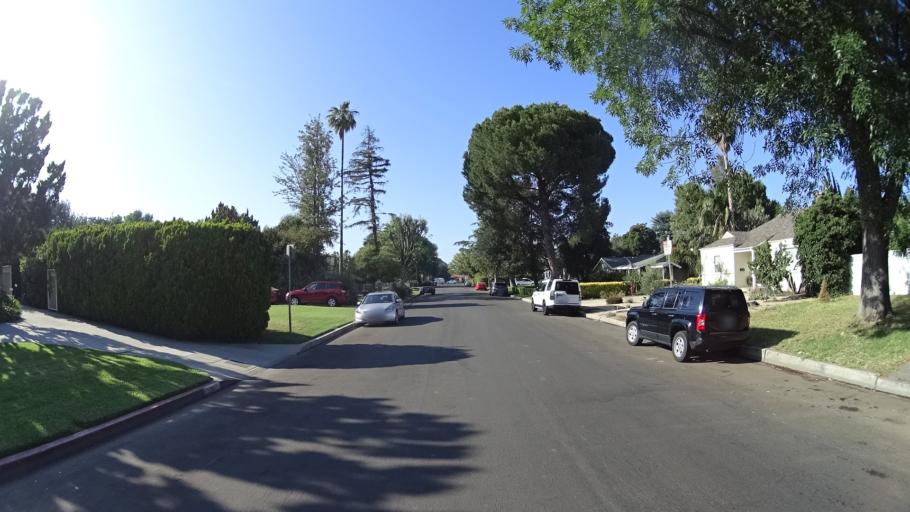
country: US
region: California
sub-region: Los Angeles County
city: Van Nuys
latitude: 34.1741
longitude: -118.4411
